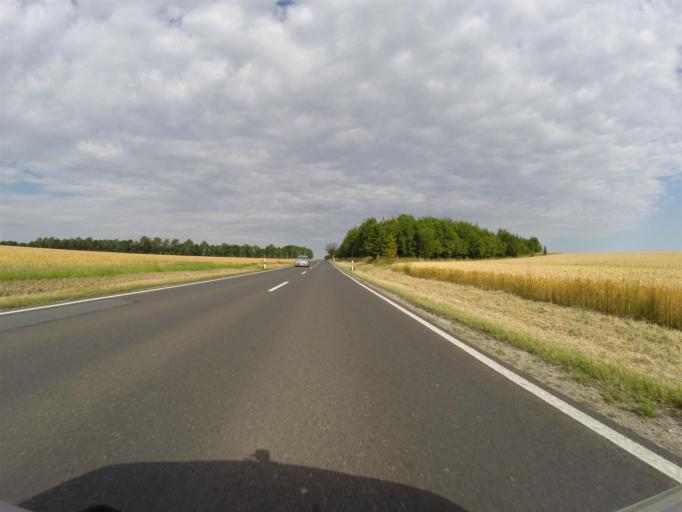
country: DE
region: Thuringia
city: Frankendorf
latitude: 50.9686
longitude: 11.4400
